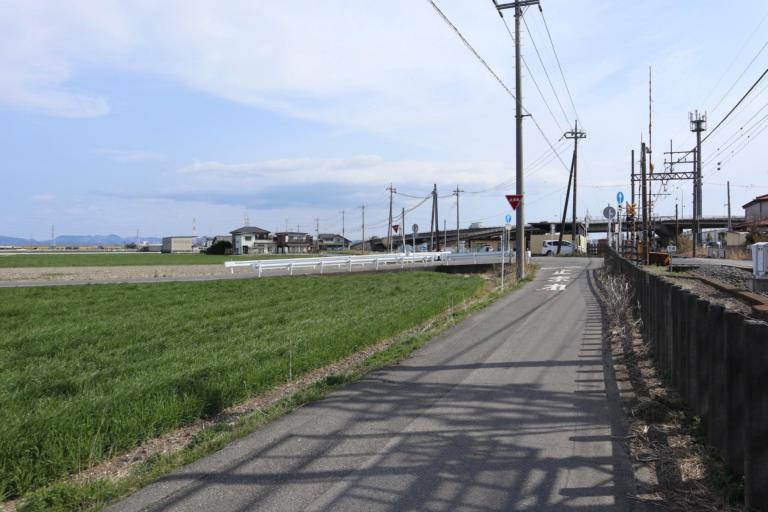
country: JP
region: Gunma
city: Tatebayashi
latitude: 36.2634
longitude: 139.5420
